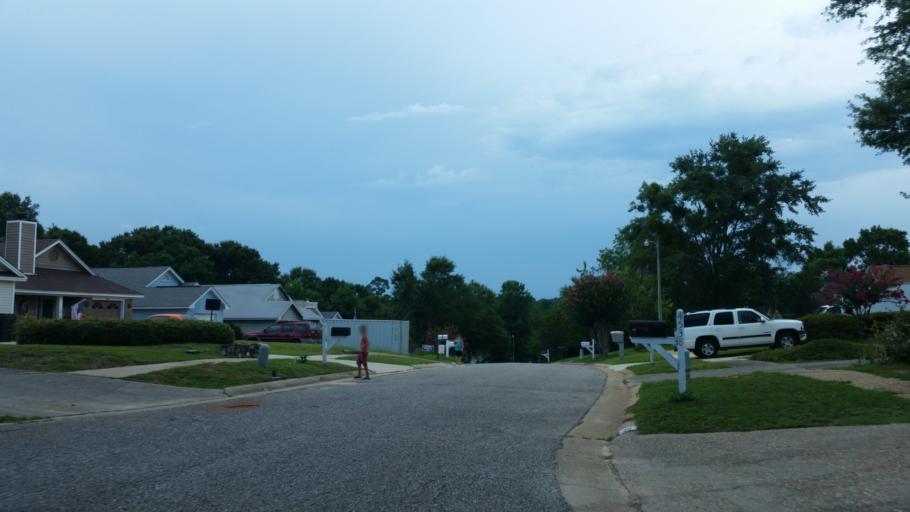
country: US
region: Florida
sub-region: Escambia County
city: Ferry Pass
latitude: 30.5054
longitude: -87.1749
